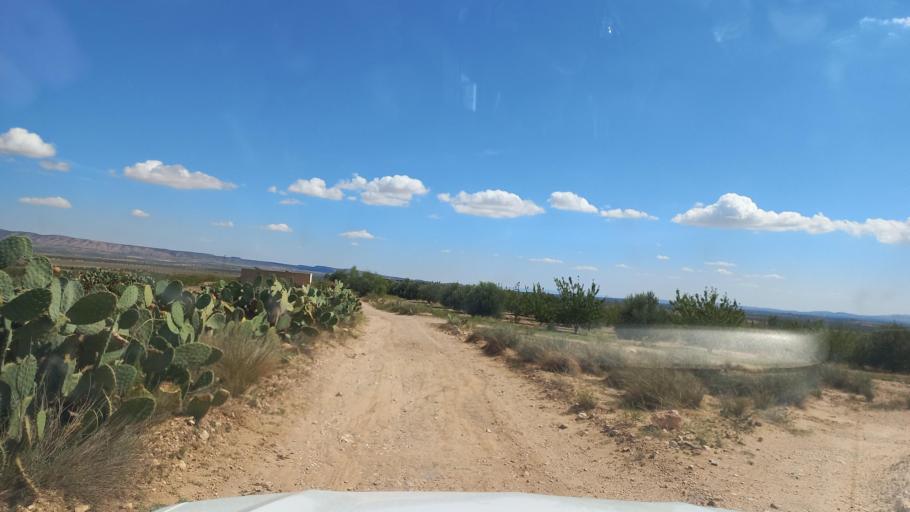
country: TN
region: Al Qasrayn
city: Sbiba
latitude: 35.3518
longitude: 9.0152
